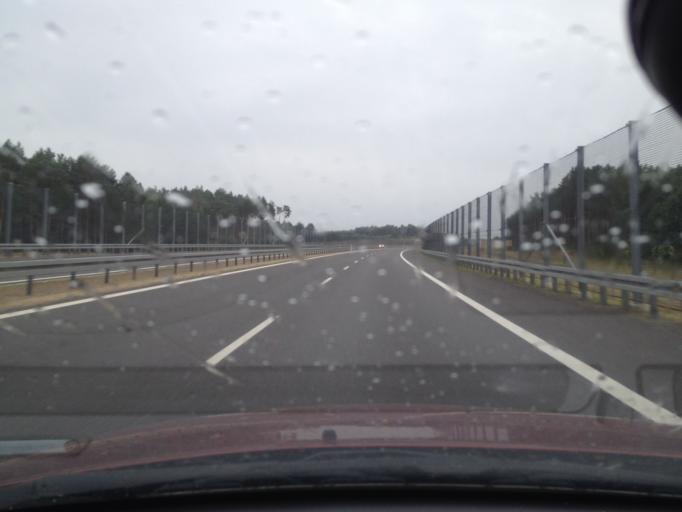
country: PL
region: Lubusz
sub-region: Powiat miedzyrzecki
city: Skwierzyna
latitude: 52.5760
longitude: 15.4679
